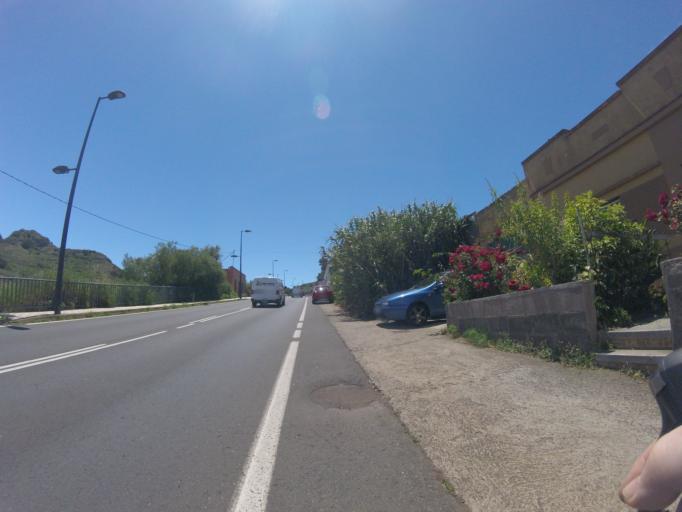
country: ES
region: Canary Islands
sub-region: Provincia de Santa Cruz de Tenerife
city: Tegueste
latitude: 28.5157
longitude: -16.3176
